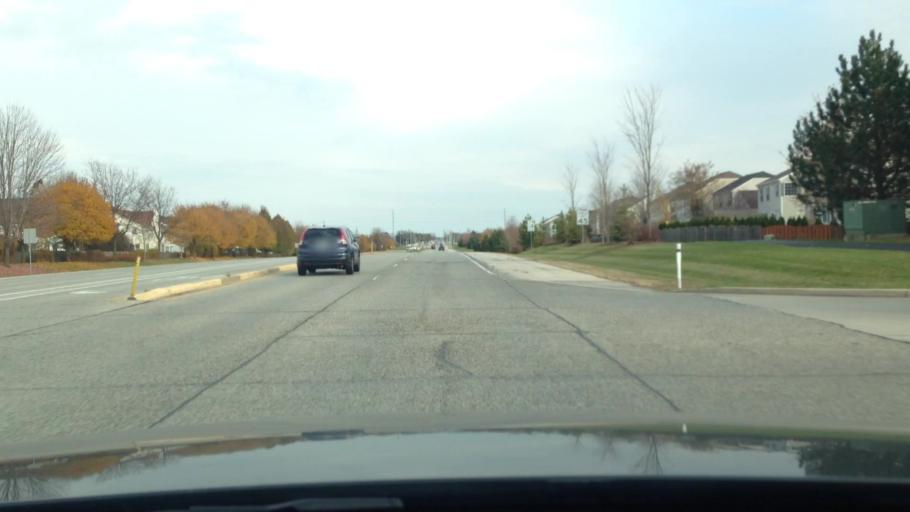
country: US
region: Illinois
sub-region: McHenry County
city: Huntley
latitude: 42.1754
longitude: -88.4128
